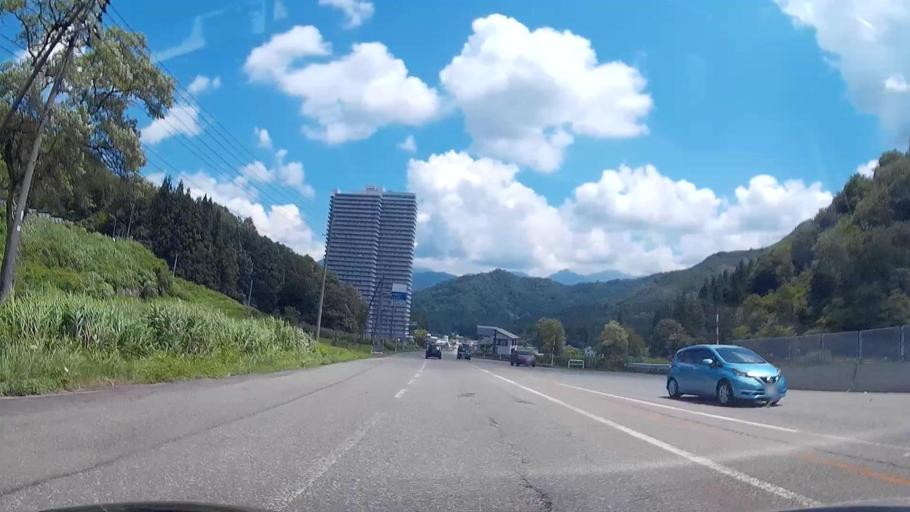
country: JP
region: Niigata
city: Shiozawa
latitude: 36.9211
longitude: 138.8128
